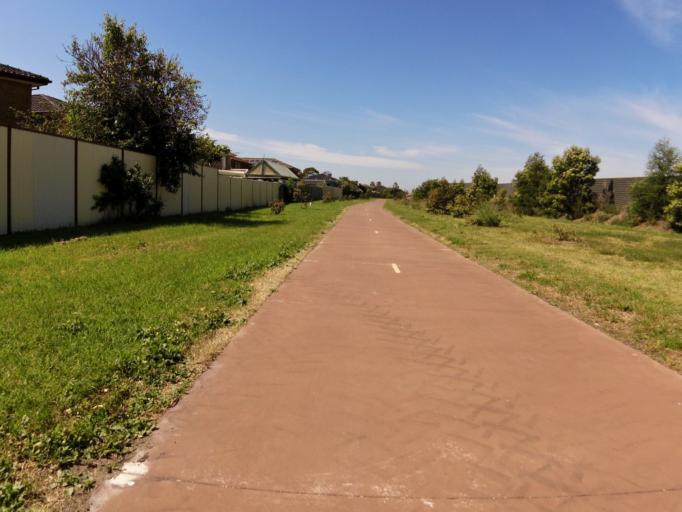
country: AU
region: Victoria
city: Heatherton
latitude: -37.9453
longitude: 145.0987
